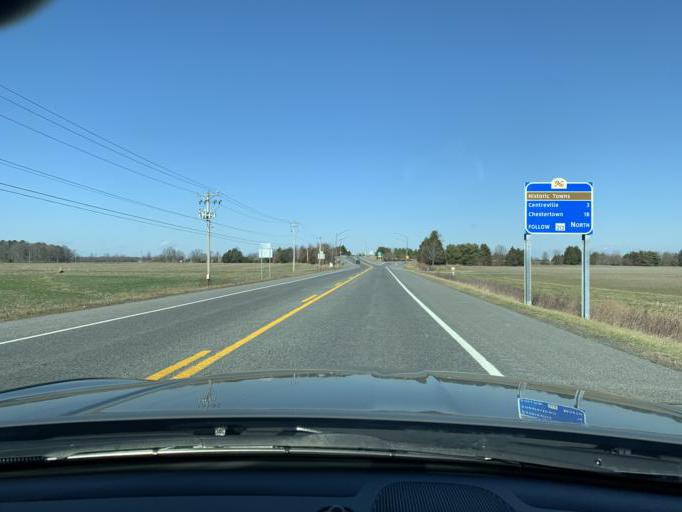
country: US
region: Maryland
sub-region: Queen Anne's County
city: Centreville
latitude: 39.0097
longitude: -76.0753
